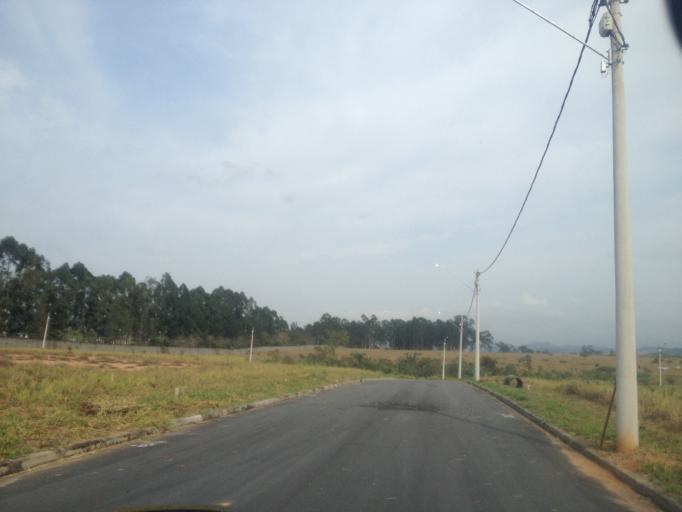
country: BR
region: Rio de Janeiro
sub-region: Porto Real
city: Porto Real
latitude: -22.4206
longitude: -44.3120
